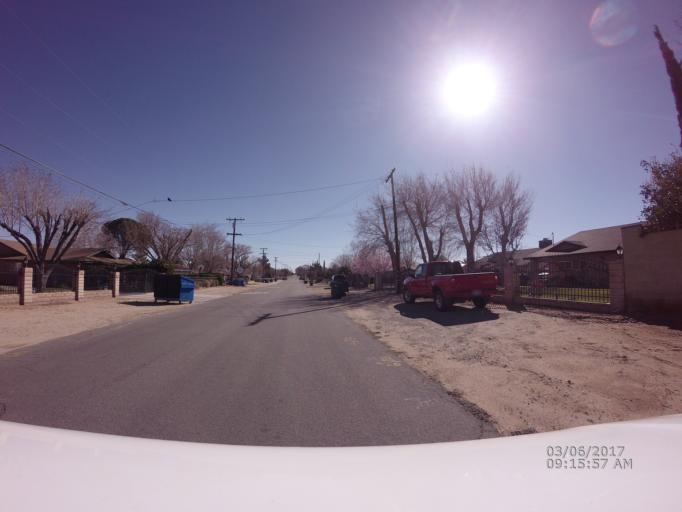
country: US
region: California
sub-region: Los Angeles County
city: Quartz Hill
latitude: 34.6547
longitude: -118.2095
